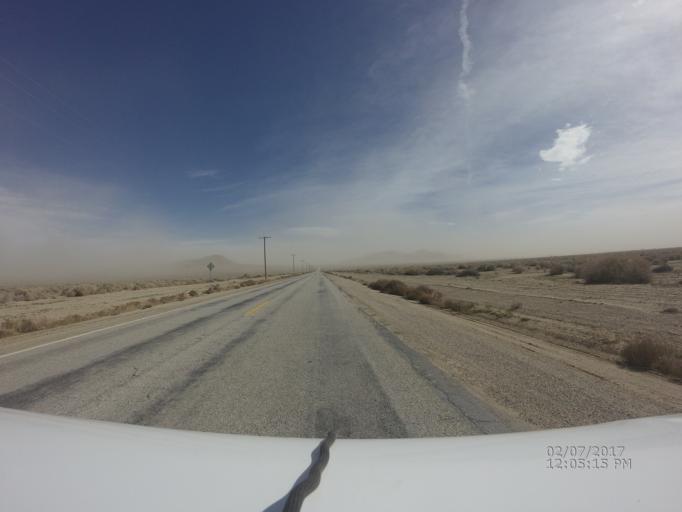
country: US
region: California
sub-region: Los Angeles County
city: Lake Los Angeles
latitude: 34.6901
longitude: -117.8604
